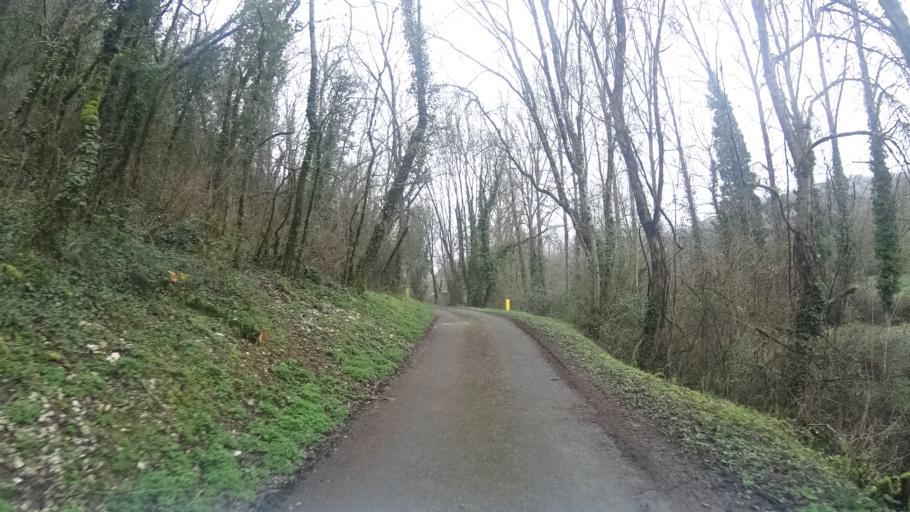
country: FR
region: Aquitaine
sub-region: Departement de la Dordogne
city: Terrasson-Lavilledieu
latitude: 45.1090
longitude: 1.2392
